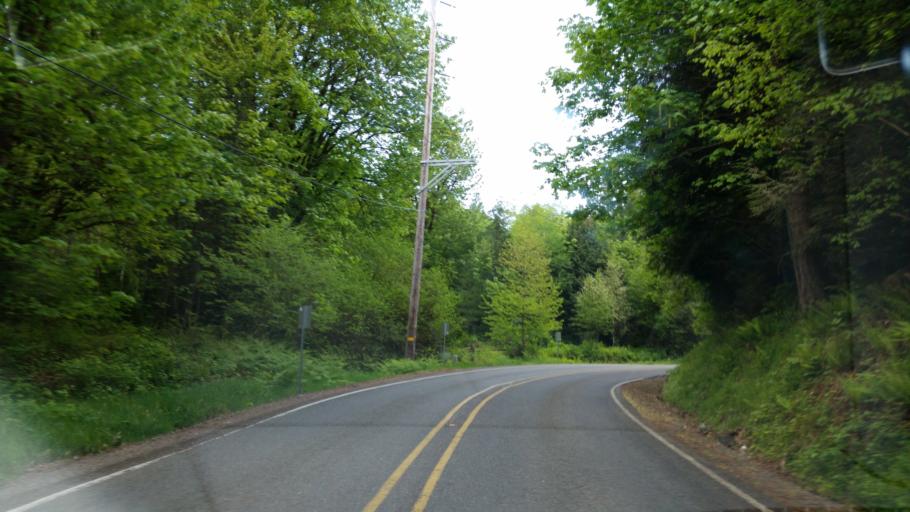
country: US
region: Washington
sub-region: Pierce County
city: Key Center
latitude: 47.3389
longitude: -122.7633
